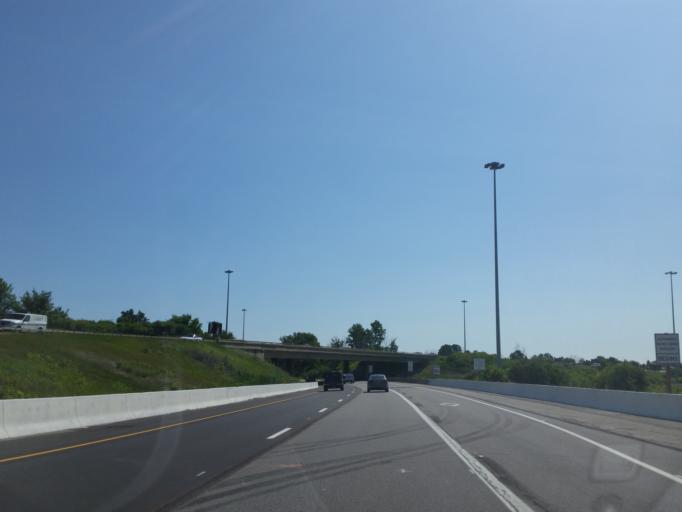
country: CA
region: Ontario
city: Ottawa
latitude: 45.4229
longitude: -75.6214
